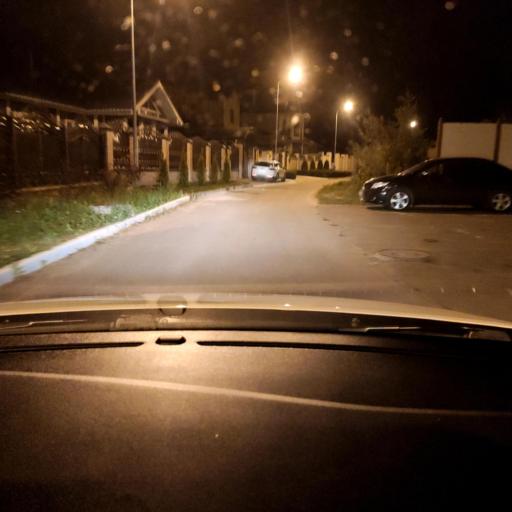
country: RU
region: Tatarstan
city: Osinovo
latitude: 55.8598
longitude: 48.7936
